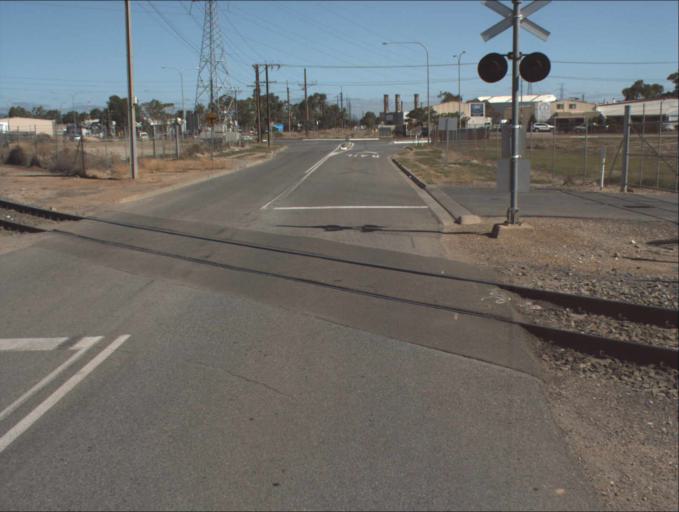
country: AU
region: South Australia
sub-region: Port Adelaide Enfield
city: Enfield
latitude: -34.8386
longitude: 138.5817
